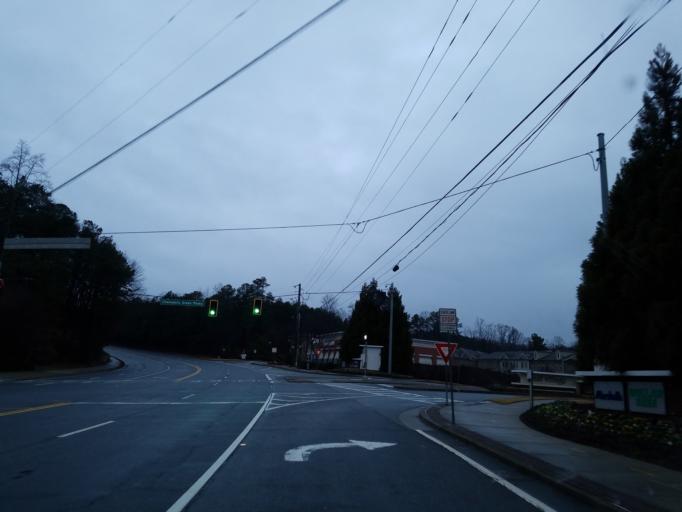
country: US
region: Georgia
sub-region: DeKalb County
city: Dunwoody
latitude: 34.0001
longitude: -84.2842
